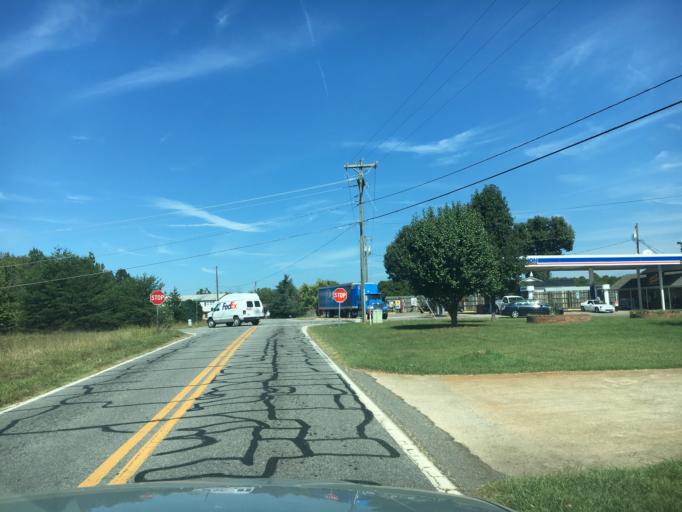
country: US
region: North Carolina
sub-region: Rutherford County
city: Spindale
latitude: 35.2984
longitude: -81.9401
